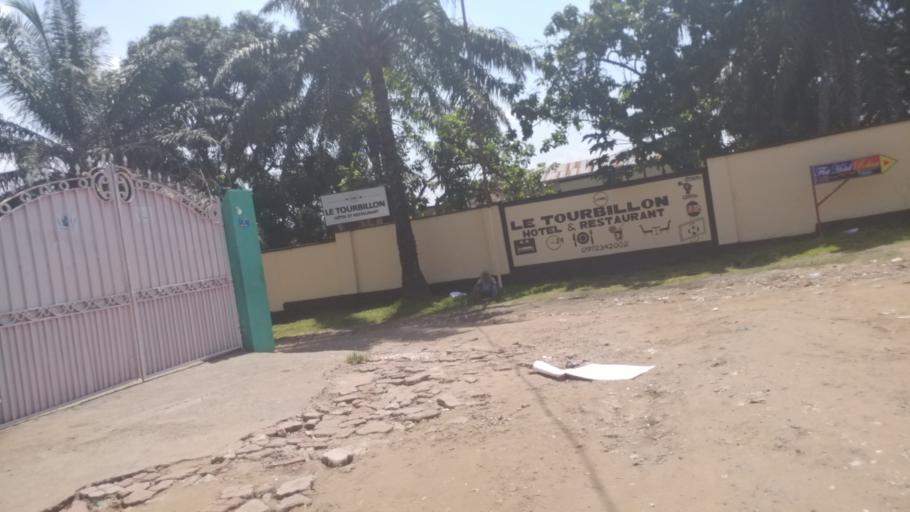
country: CD
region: Kinshasa
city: Kinshasa
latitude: -4.3456
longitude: 15.2623
